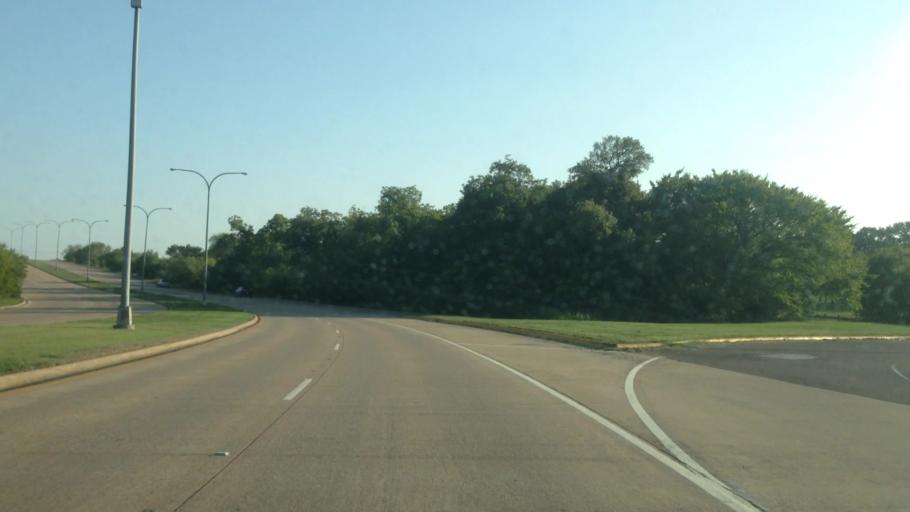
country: US
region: Texas
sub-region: Tarrant County
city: Pantego
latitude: 32.7355
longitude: -97.1809
